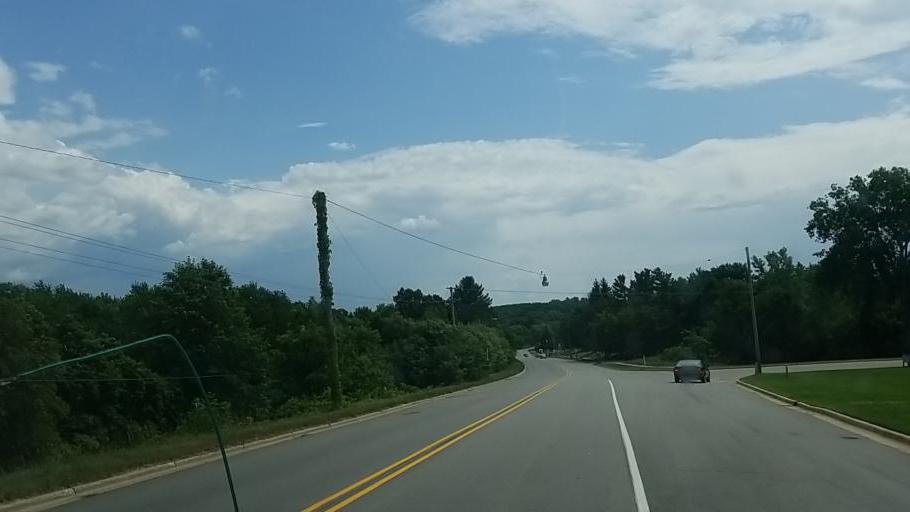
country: US
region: Michigan
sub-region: Kent County
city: Walker
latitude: 43.0062
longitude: -85.7210
